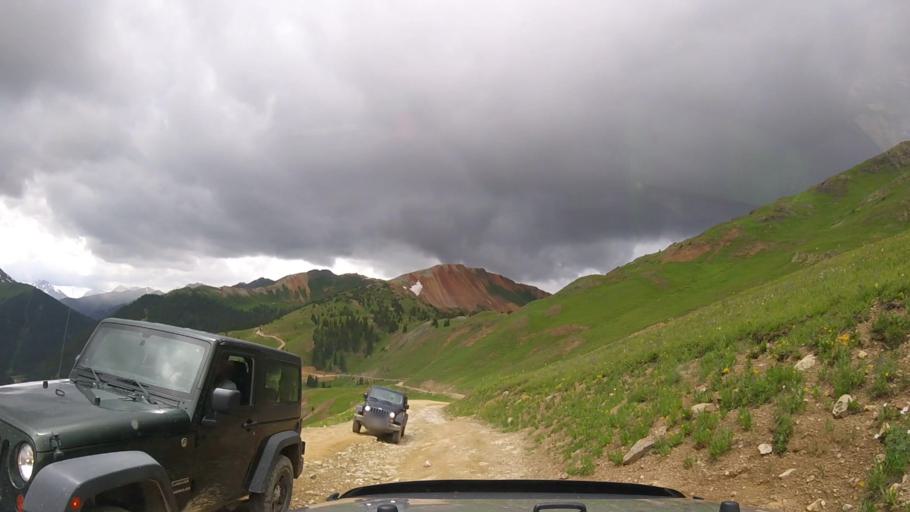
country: US
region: Colorado
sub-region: San Juan County
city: Silverton
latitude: 37.9132
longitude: -107.6394
